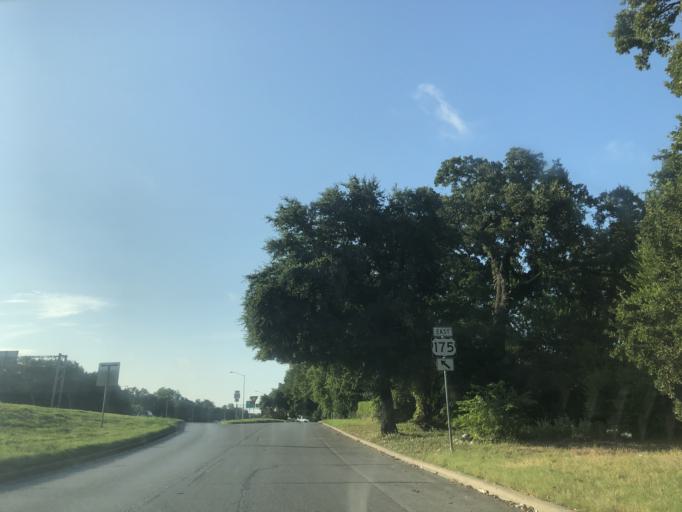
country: US
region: Texas
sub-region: Dallas County
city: Dallas
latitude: 32.7618
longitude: -96.7721
